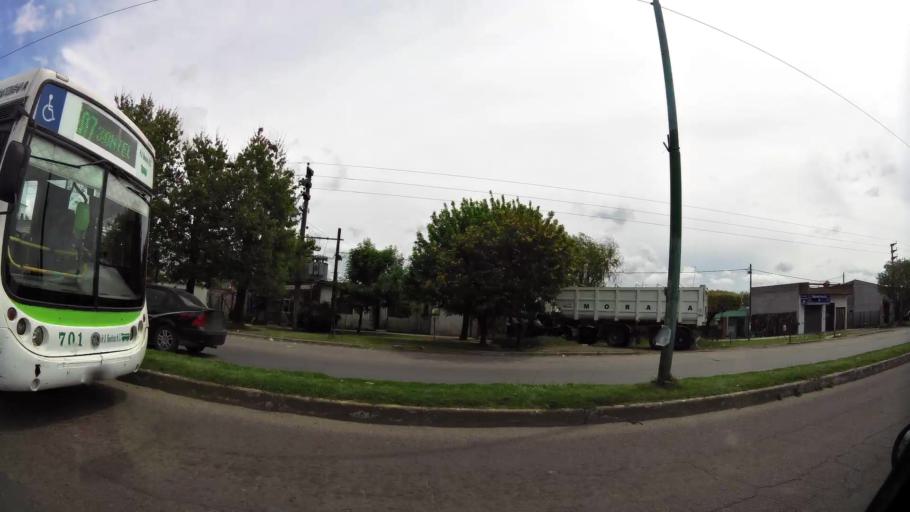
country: AR
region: Buenos Aires
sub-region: Partido de Quilmes
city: Quilmes
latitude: -34.7792
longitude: -58.2797
